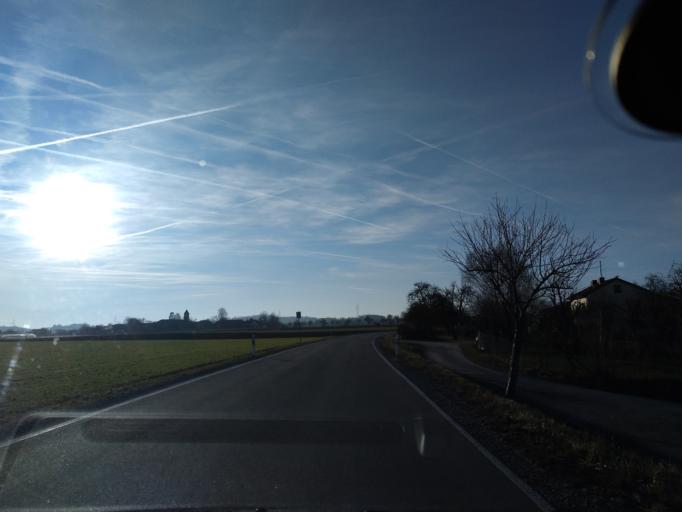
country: DE
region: Baden-Wuerttemberg
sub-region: Regierungsbezirk Stuttgart
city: Obersontheim
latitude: 49.1021
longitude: 9.9651
